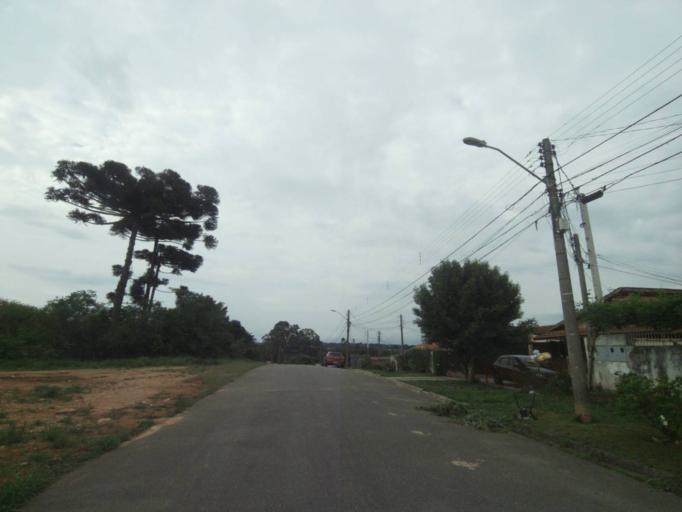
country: BR
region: Parana
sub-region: Curitiba
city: Curitiba
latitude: -25.3931
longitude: -49.2994
